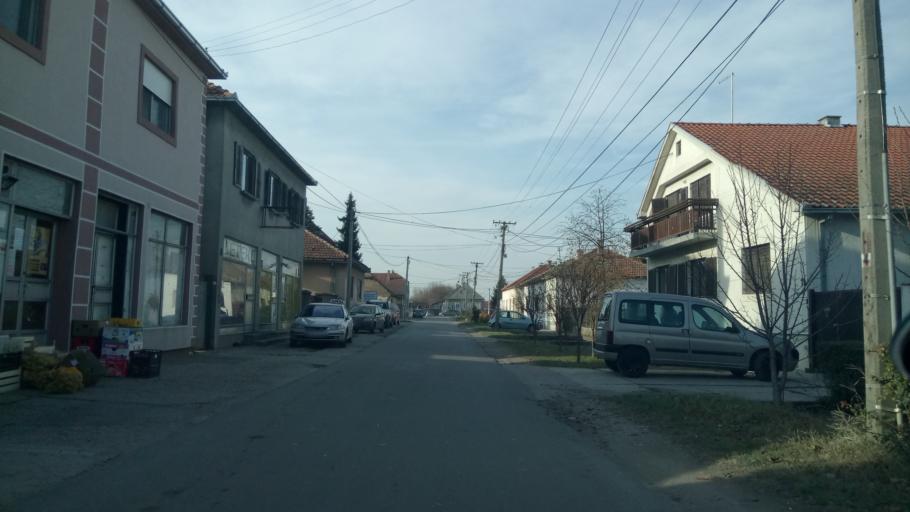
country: RS
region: Autonomna Pokrajina Vojvodina
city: Nova Pazova
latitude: 44.9450
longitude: 20.2222
